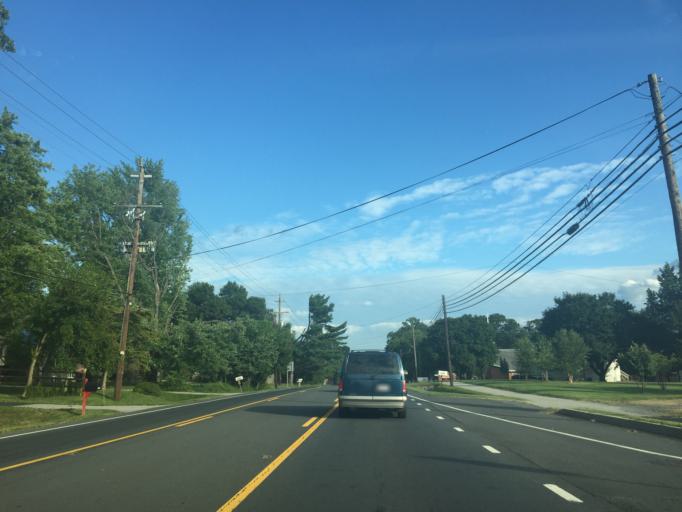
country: US
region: Maryland
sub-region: Montgomery County
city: Redland
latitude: 39.1435
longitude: -77.1409
